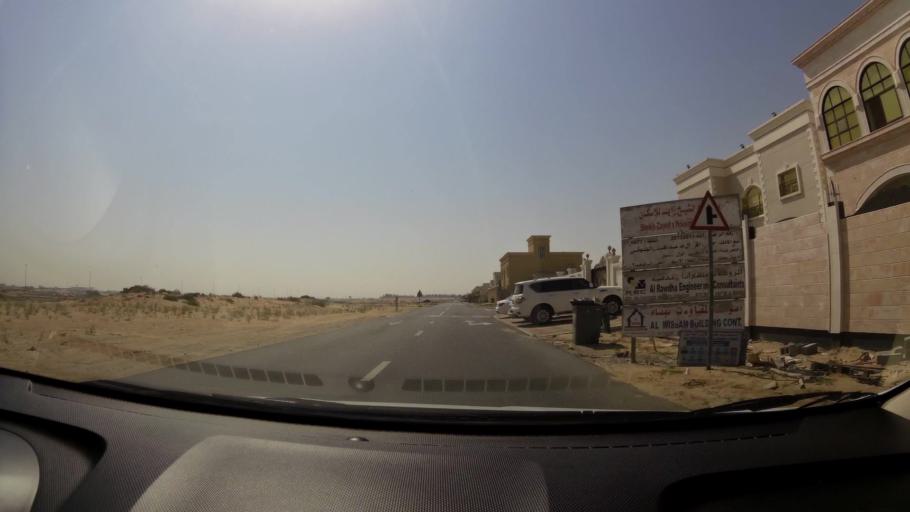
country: AE
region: Ajman
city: Ajman
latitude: 25.4151
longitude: 55.5468
